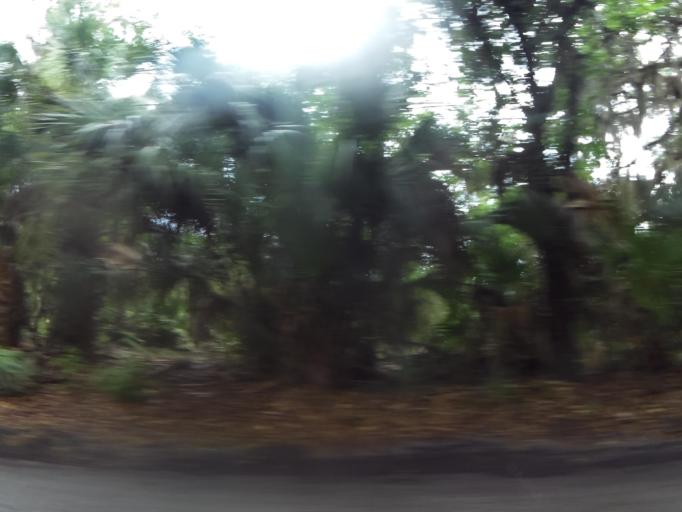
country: US
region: Florida
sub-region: Nassau County
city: Fernandina Beach
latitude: 30.6857
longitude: -81.4375
